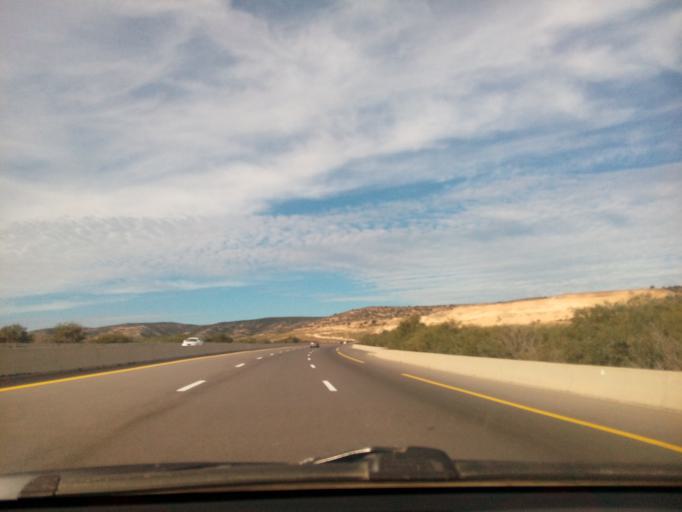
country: DZ
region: Sidi Bel Abbes
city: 'Ain el Berd
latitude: 35.4361
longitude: -0.4347
